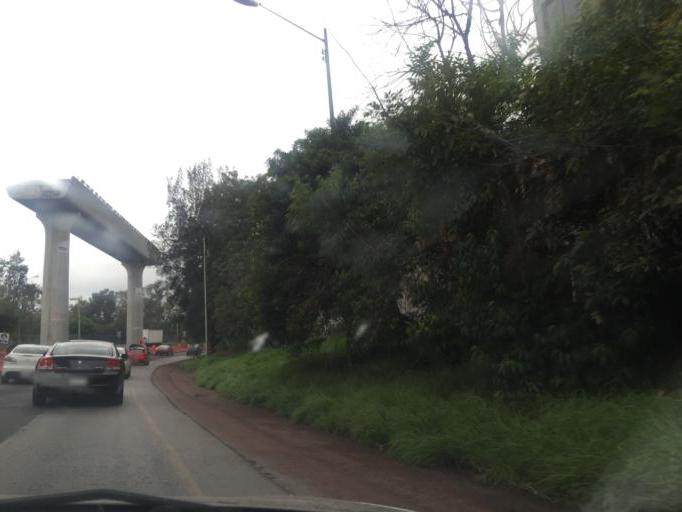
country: MX
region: Mexico City
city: Tlalpan
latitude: 19.2540
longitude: -99.1569
